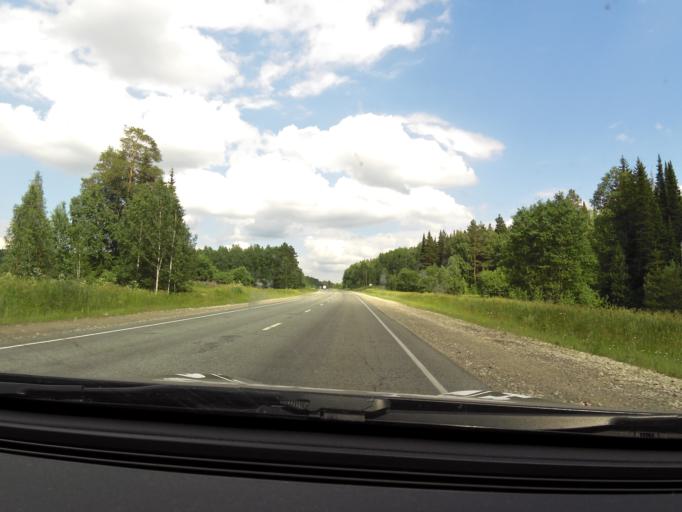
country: RU
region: Sverdlovsk
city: Bisert'
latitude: 56.8282
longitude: 59.1114
